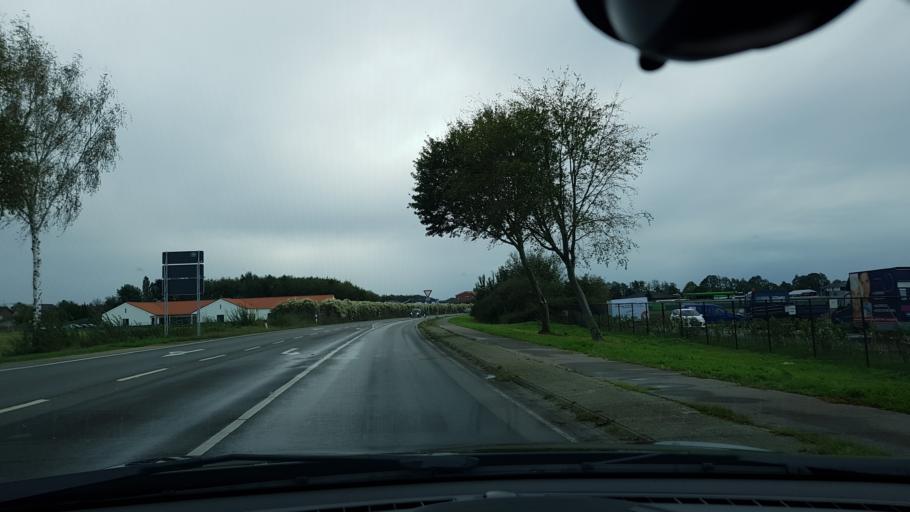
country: DE
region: North Rhine-Westphalia
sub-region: Regierungsbezirk Koln
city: Wassenberg
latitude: 51.1021
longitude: 6.1463
